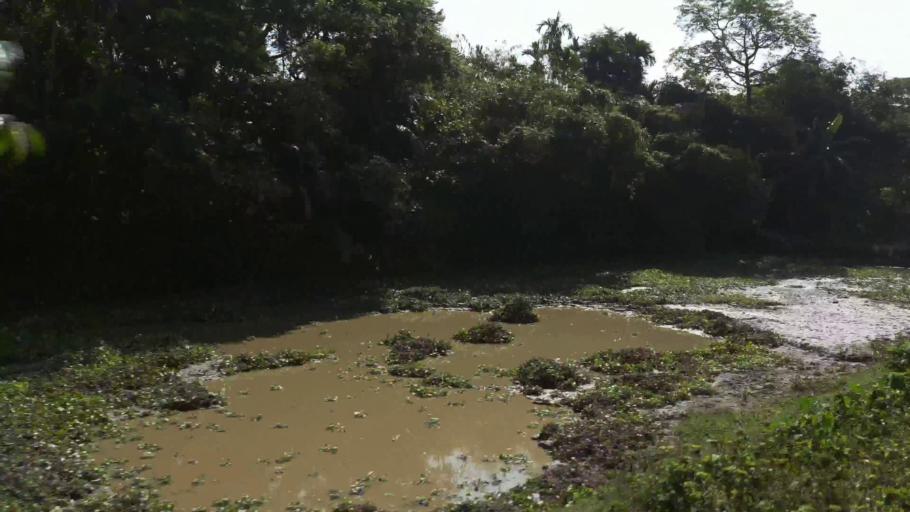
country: BD
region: Dhaka
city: Gafargaon
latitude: 24.5041
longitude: 90.5184
